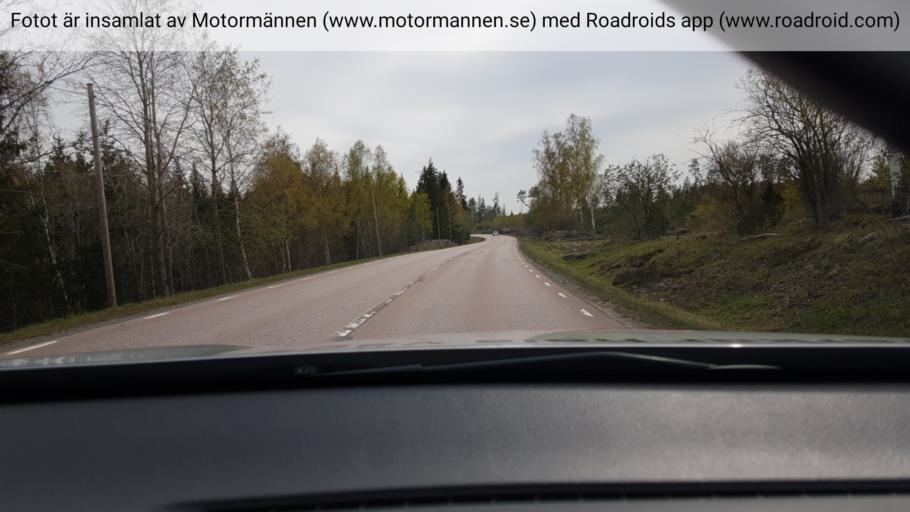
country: SE
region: Stockholm
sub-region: Norrtalje Kommun
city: Nykvarn
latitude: 59.8407
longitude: 18.0507
